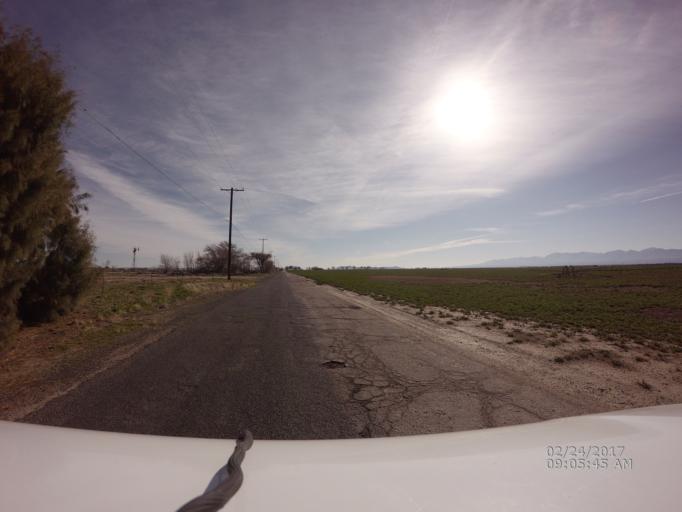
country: US
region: California
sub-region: Los Angeles County
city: Lancaster
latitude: 34.6607
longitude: -118.0528
